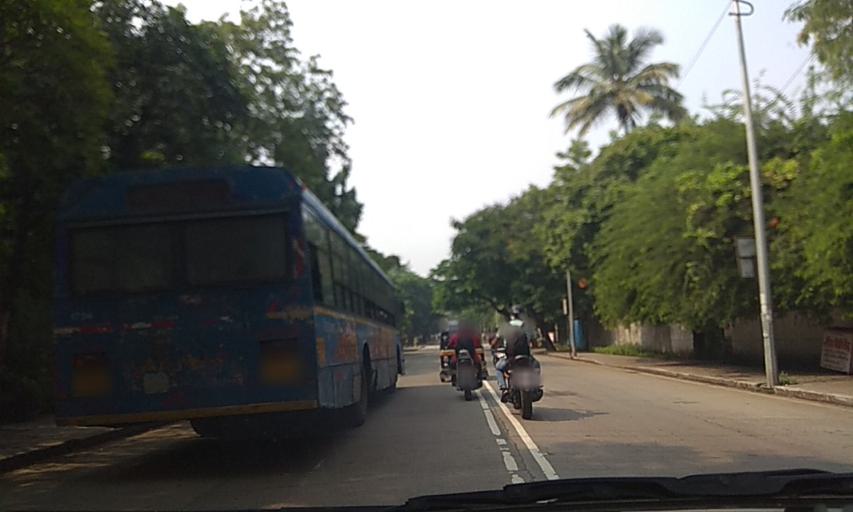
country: IN
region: Maharashtra
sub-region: Pune Division
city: Shivaji Nagar
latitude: 18.5407
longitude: 73.8362
